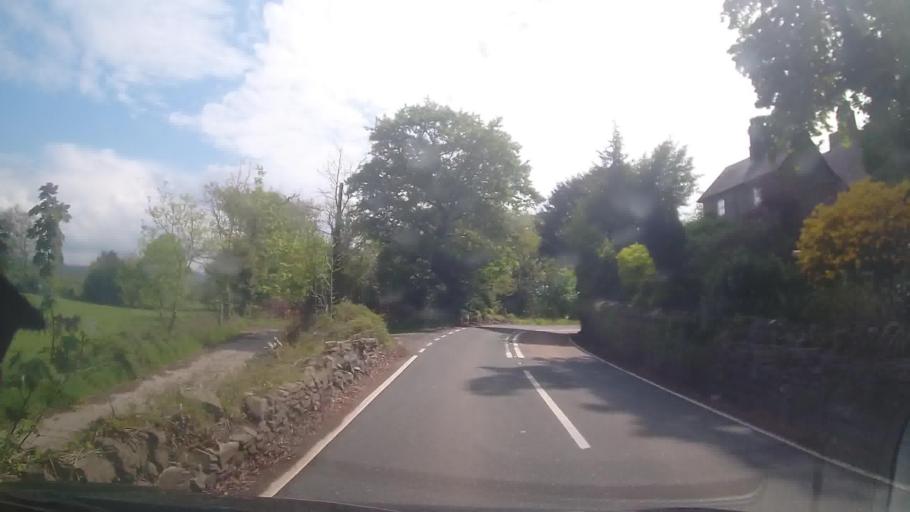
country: GB
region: Wales
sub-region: Gwynedd
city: Porthmadog
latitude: 52.9457
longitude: -4.1139
